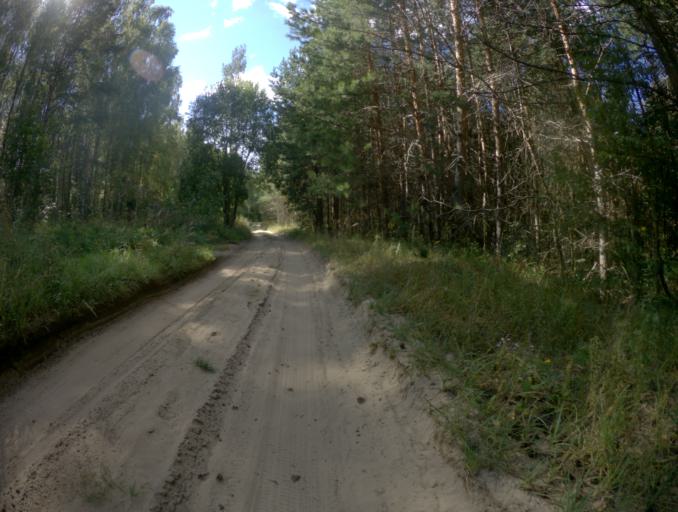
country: RU
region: Vladimir
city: Krasnaya Gorbatka
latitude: 55.8612
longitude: 41.8240
